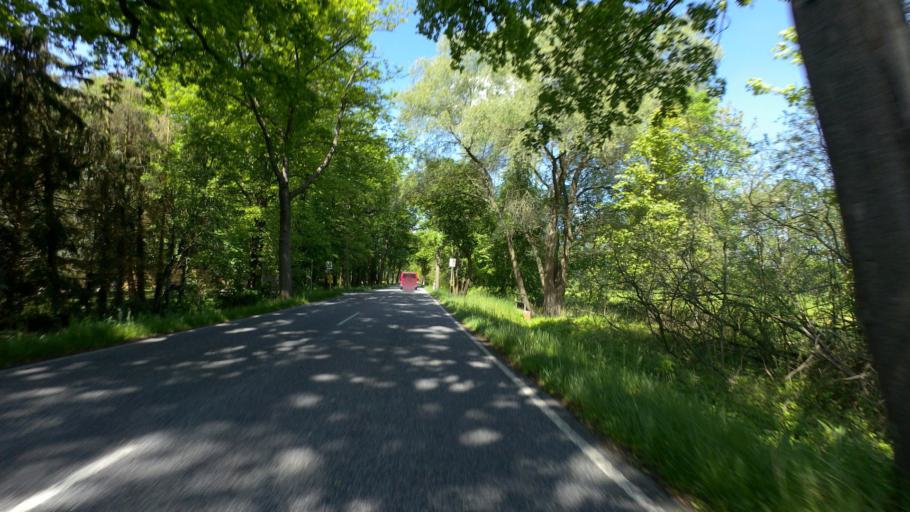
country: DE
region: Brandenburg
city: Luckau
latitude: 51.8440
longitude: 13.7439
